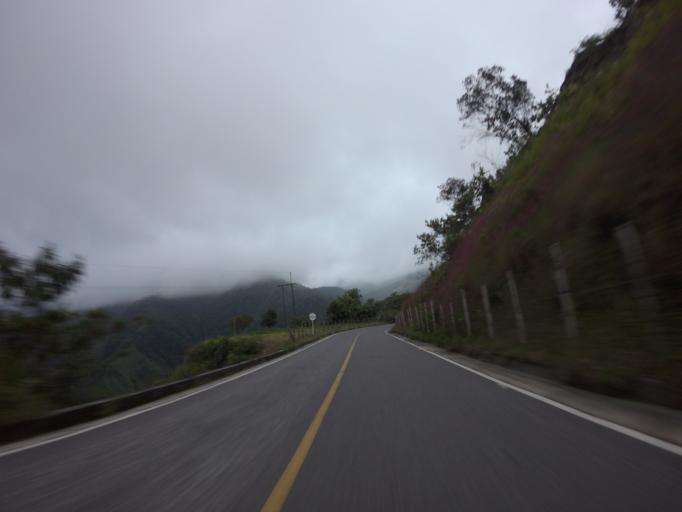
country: CO
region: Caldas
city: Manzanares
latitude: 5.3131
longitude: -75.1329
